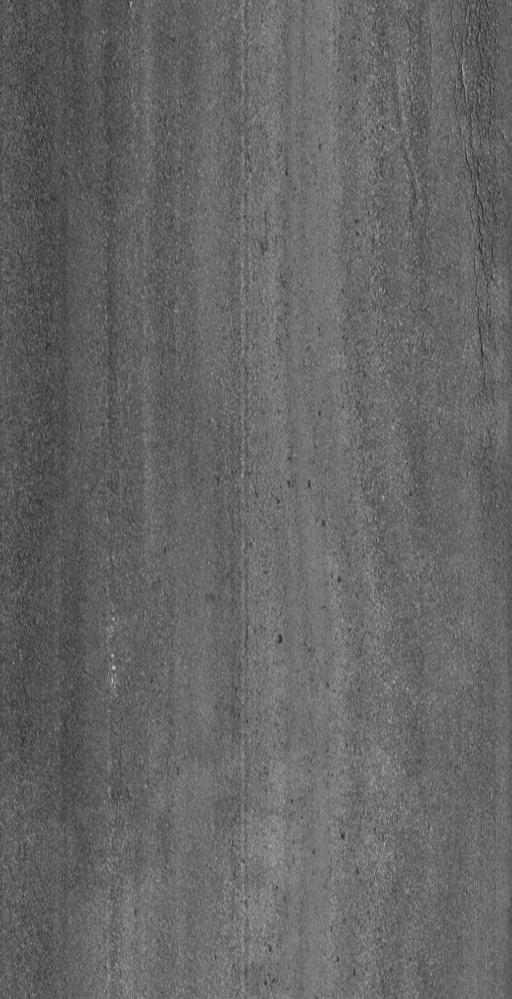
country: US
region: Vermont
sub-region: Rutland County
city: Rutland
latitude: 43.5618
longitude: -72.9393
